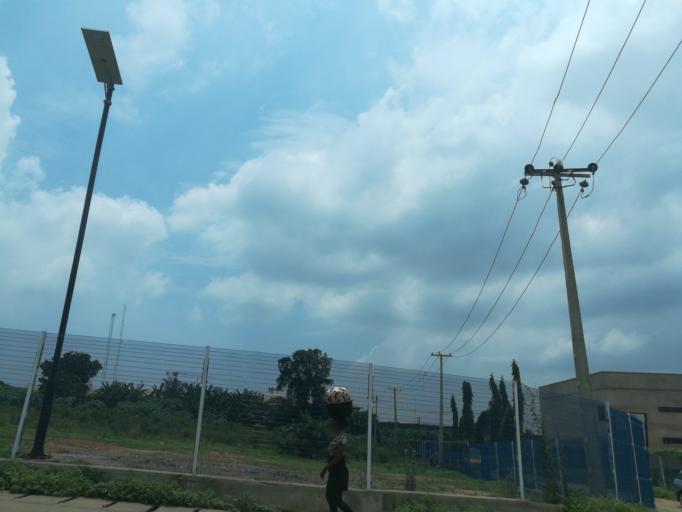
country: NG
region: Lagos
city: Ojota
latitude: 6.5968
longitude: 3.3660
